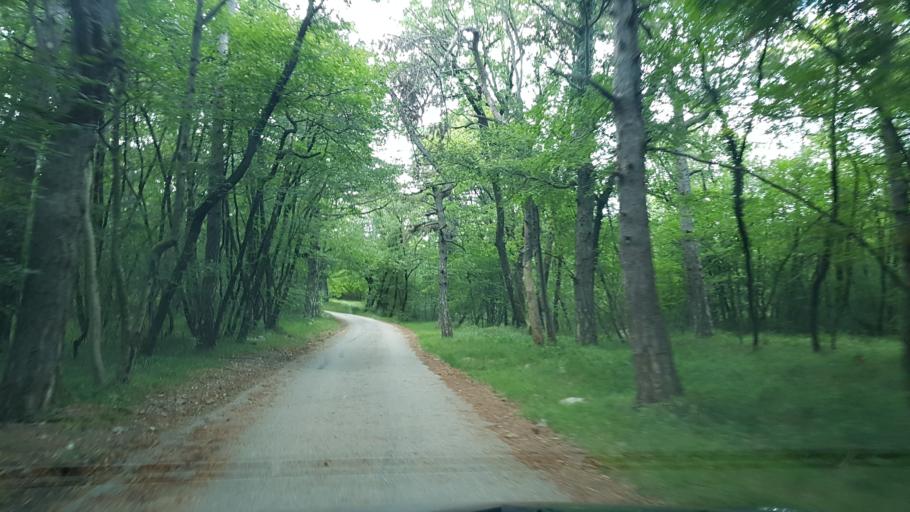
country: SI
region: Nova Gorica
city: Prvacina
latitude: 45.8560
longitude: 13.7060
